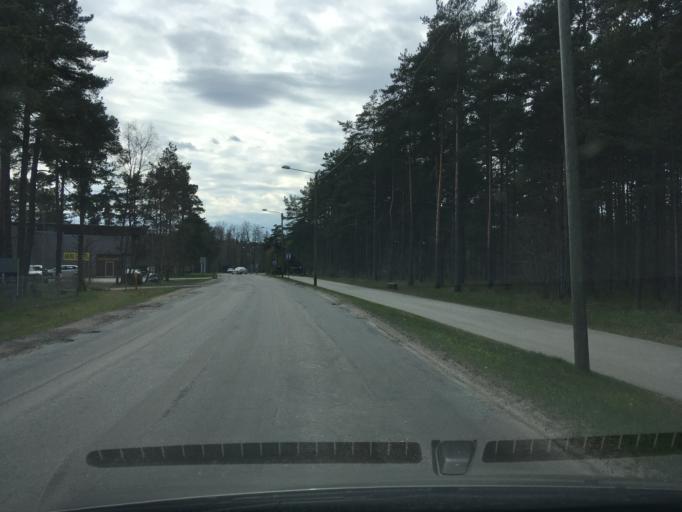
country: EE
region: Harju
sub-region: Tallinna linn
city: Kose
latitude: 59.4755
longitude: 24.9165
